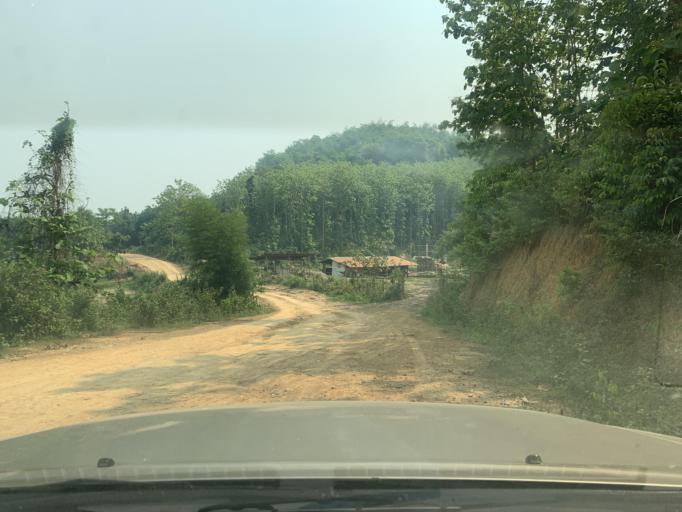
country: LA
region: Louangphabang
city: Xiang Ngeun
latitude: 19.7936
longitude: 102.1987
